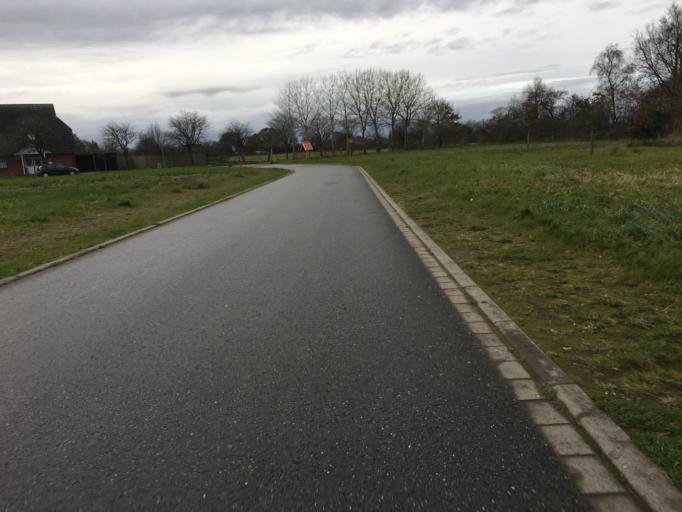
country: DE
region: Schleswig-Holstein
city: Wanderup
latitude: 54.6948
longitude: 9.3389
